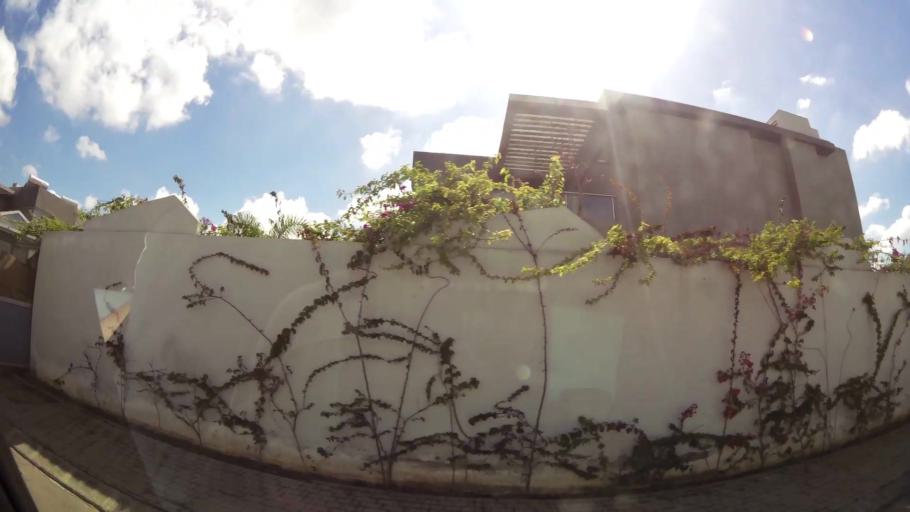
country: MA
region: Grand Casablanca
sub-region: Nouaceur
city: Bouskoura
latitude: 33.4700
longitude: -7.5983
